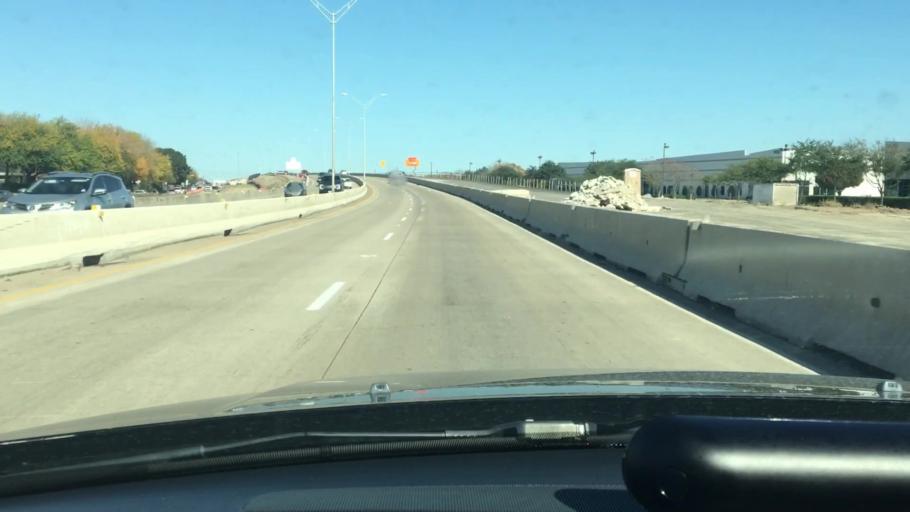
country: US
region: Texas
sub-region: Harris County
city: Deer Park
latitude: 29.6863
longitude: -95.1538
